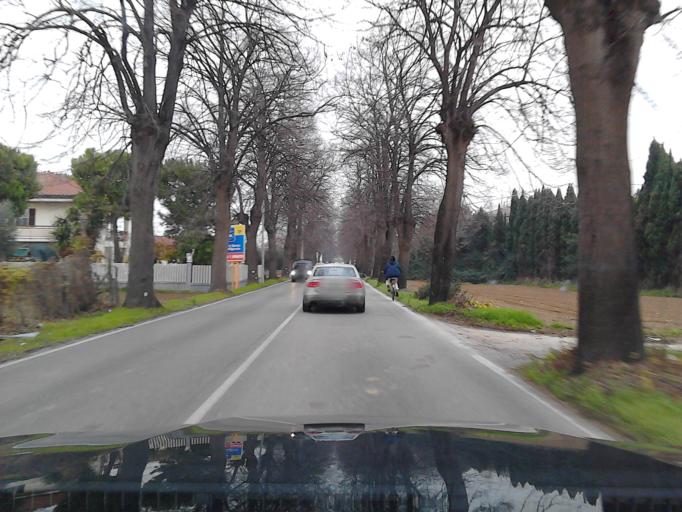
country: IT
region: Abruzzo
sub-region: Provincia di Teramo
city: Alba Adriatica
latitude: 42.8342
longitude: 13.9074
